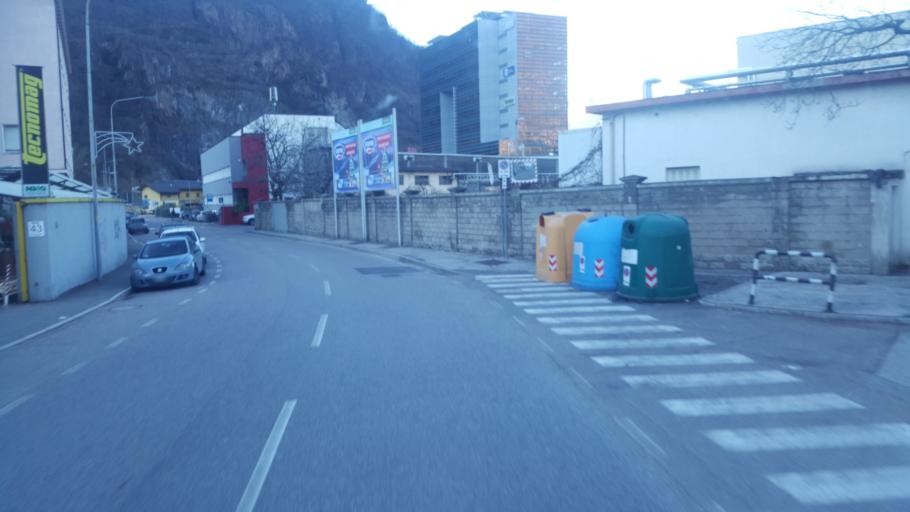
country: IT
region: Trentino-Alto Adige
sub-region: Bolzano
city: Bolzano
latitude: 46.4937
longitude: 11.3642
